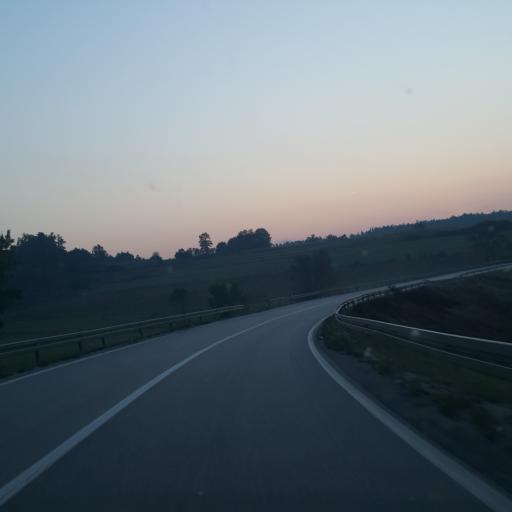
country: RS
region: Central Serbia
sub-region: Nisavski Okrug
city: Svrljig
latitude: 43.4534
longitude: 22.1935
